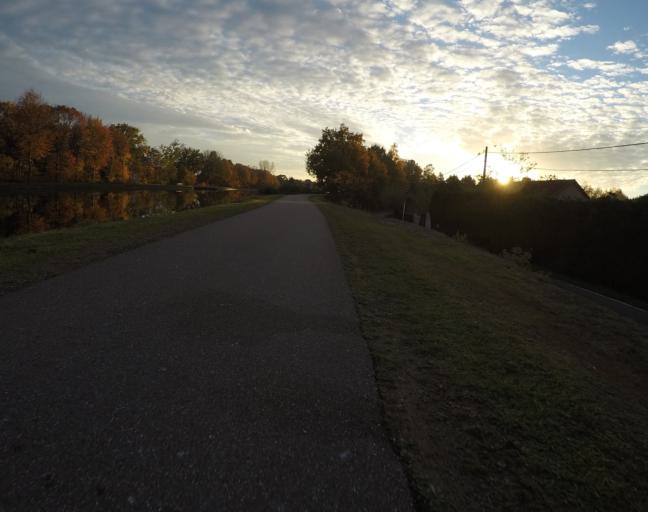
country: BE
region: Flanders
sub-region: Provincie Antwerpen
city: Geel
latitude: 51.1950
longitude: 4.9604
